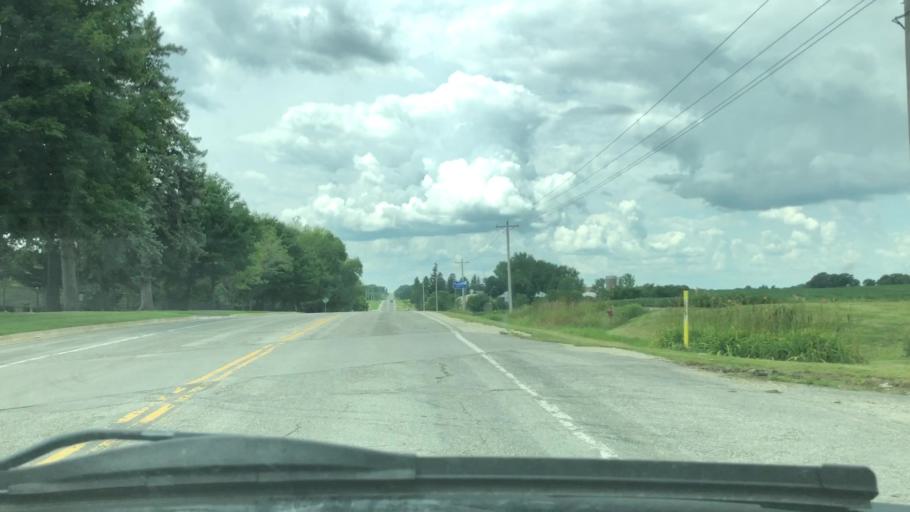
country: US
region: Minnesota
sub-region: Olmsted County
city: Stewartville
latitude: 43.8628
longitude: -92.4936
